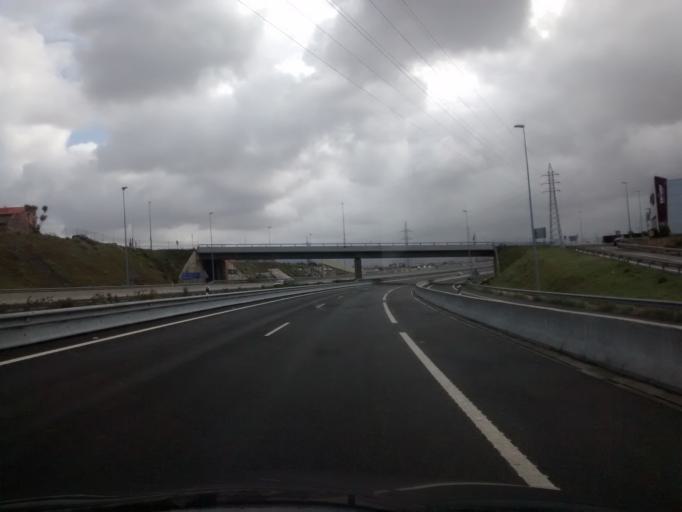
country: ES
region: Cantabria
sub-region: Provincia de Cantabria
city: Santa Cruz de Bezana
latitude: 43.4442
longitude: -3.8777
